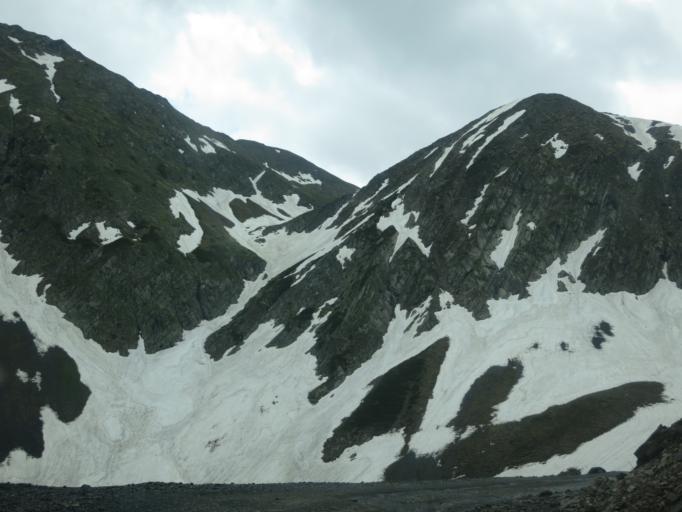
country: GE
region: Kakheti
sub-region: Telavi
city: Telavi
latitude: 42.2840
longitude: 45.5088
